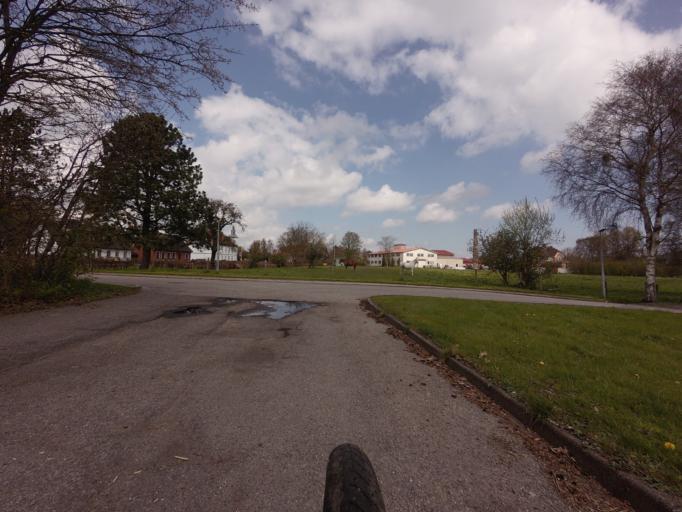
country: DK
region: North Denmark
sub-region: Alborg Kommune
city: Klarup
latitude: 56.9357
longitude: 10.0574
